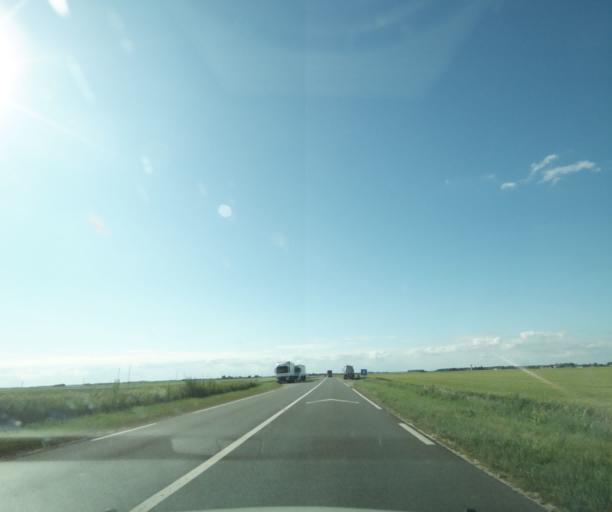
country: FR
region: Centre
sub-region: Departement d'Eure-et-Loir
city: Janville
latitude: 48.2118
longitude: 1.8155
